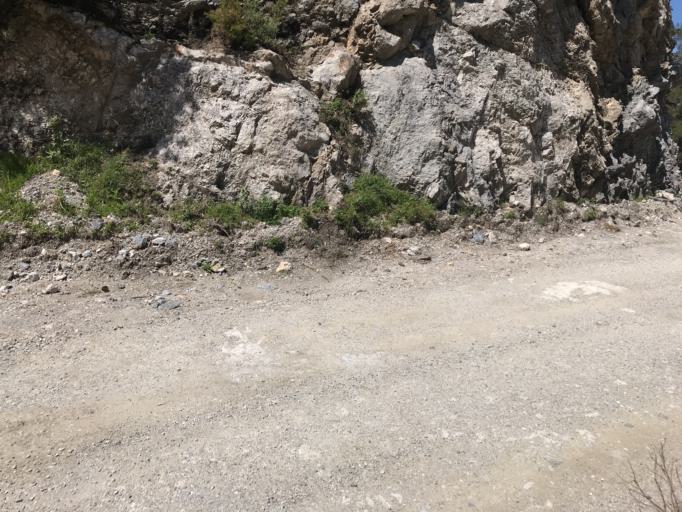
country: ES
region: Andalusia
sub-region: Provincia de Malaga
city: Alcaucin
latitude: 36.9162
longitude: -4.0968
